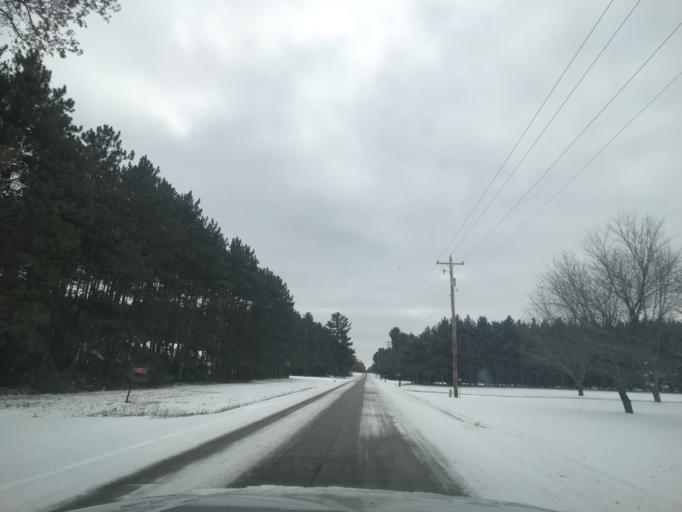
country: US
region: Wisconsin
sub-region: Brown County
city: Suamico
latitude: 44.6889
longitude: -88.1110
